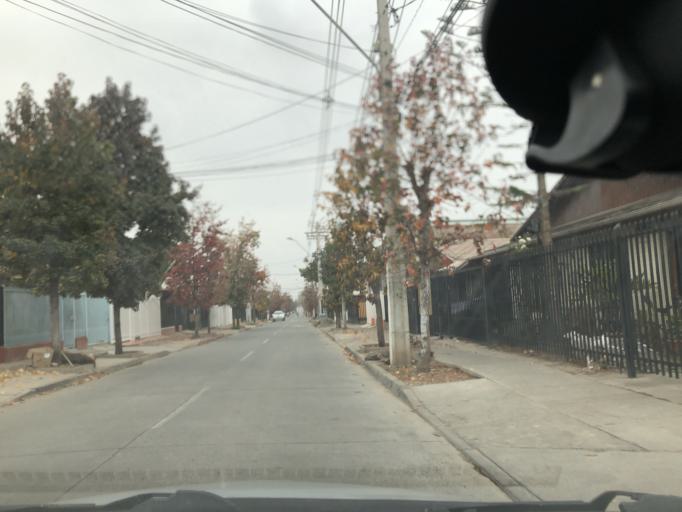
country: CL
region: Santiago Metropolitan
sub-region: Provincia de Santiago
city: La Pintana
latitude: -33.5790
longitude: -70.6043
